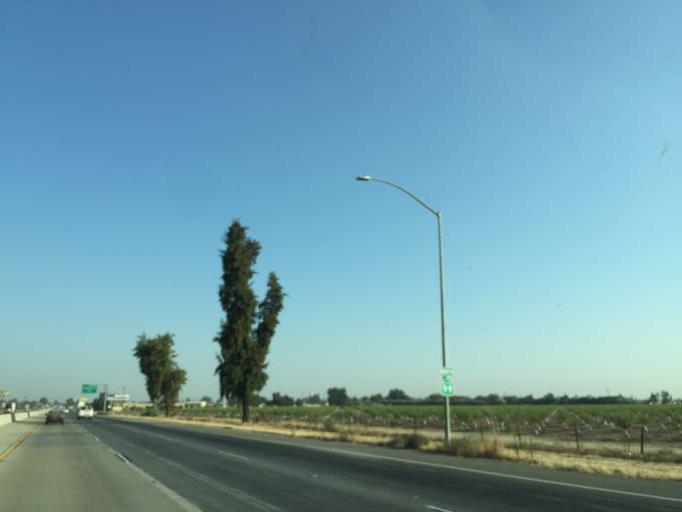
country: US
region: California
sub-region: Fresno County
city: Selma
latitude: 36.5500
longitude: -119.5997
